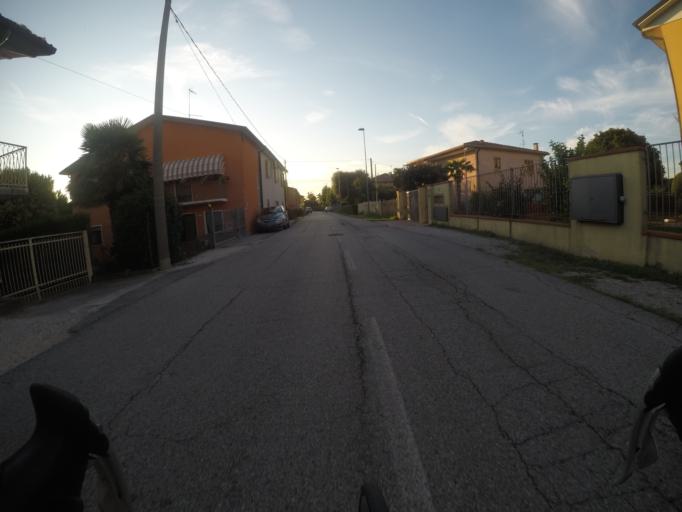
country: IT
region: Veneto
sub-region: Provincia di Rovigo
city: Fratta Polesine
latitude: 45.0282
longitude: 11.6508
